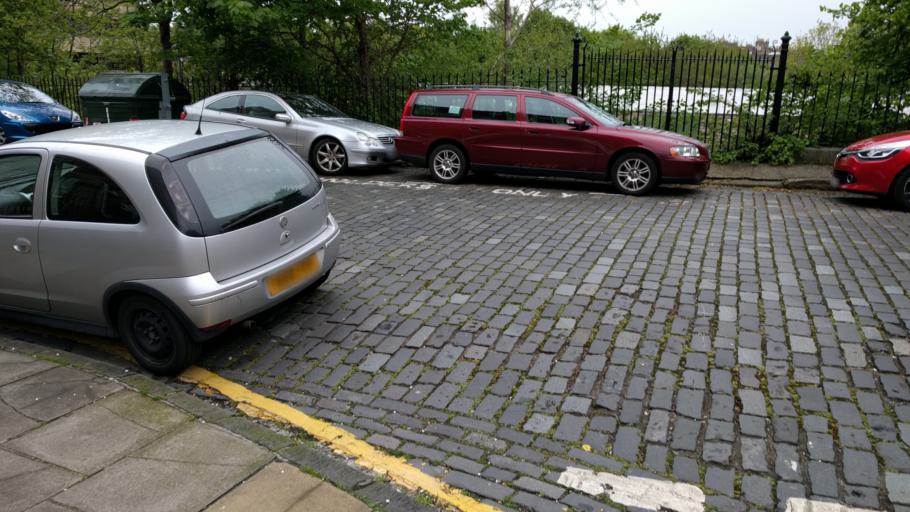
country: GB
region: Scotland
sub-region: Edinburgh
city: Edinburgh
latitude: 55.9595
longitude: -3.1971
